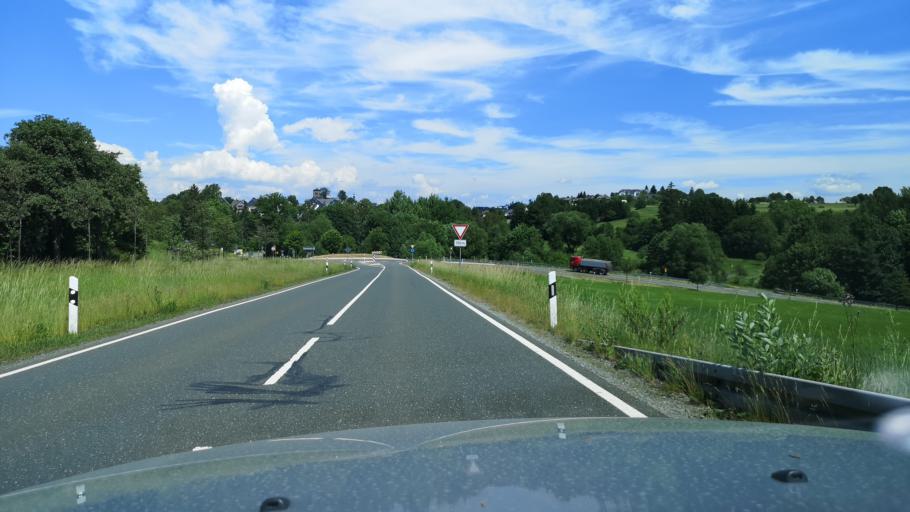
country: DE
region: Bavaria
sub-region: Upper Franconia
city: Teuschnitz
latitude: 50.3902
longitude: 11.3781
